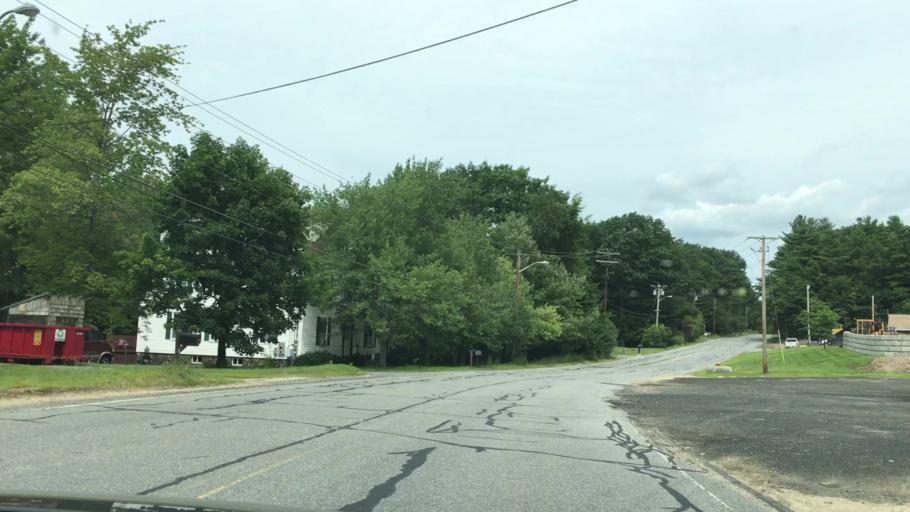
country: US
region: Massachusetts
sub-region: Worcester County
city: Winchendon
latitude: 42.6845
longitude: -72.0218
